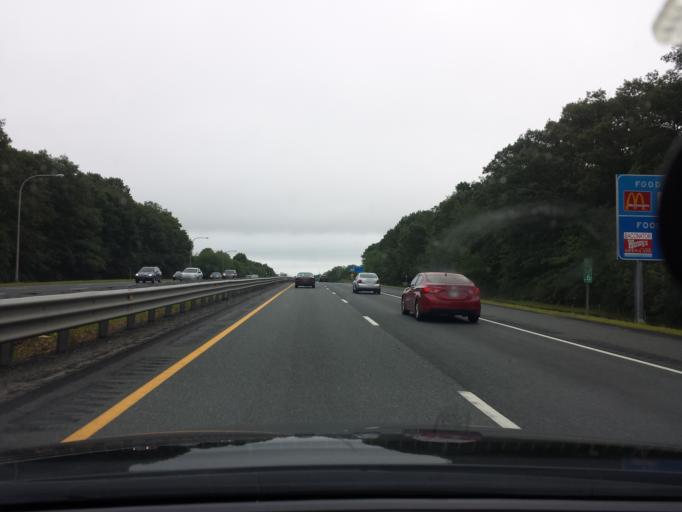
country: US
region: Rhode Island
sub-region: Kent County
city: West Warwick
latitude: 41.6663
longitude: -71.5082
